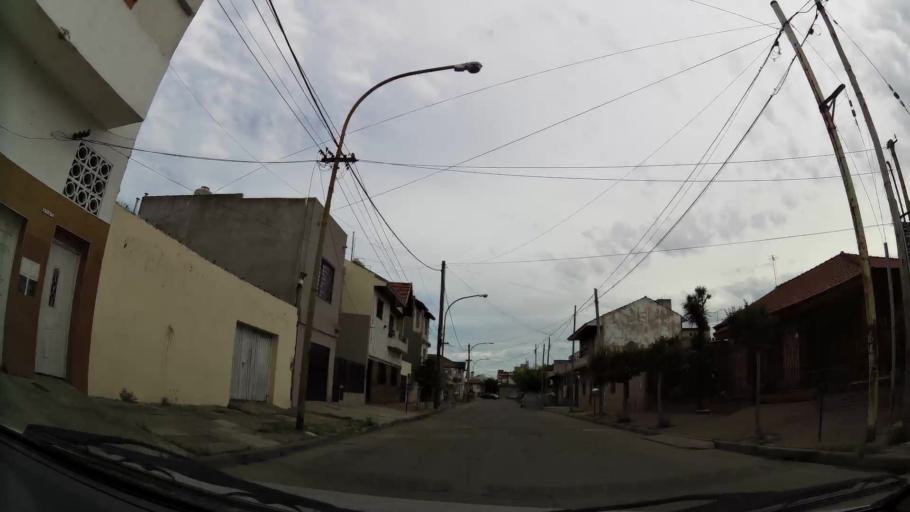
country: AR
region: Buenos Aires
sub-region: Partido de Lanus
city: Lanus
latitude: -34.6751
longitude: -58.3996
